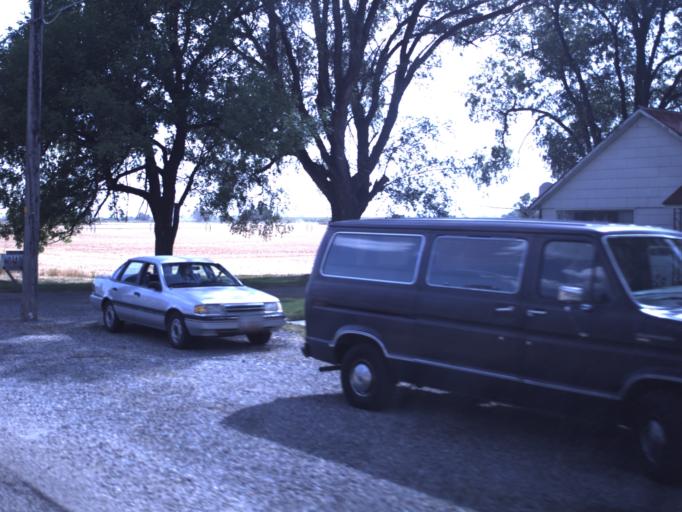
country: US
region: Utah
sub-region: Box Elder County
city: Honeyville
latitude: 41.6836
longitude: -112.0899
